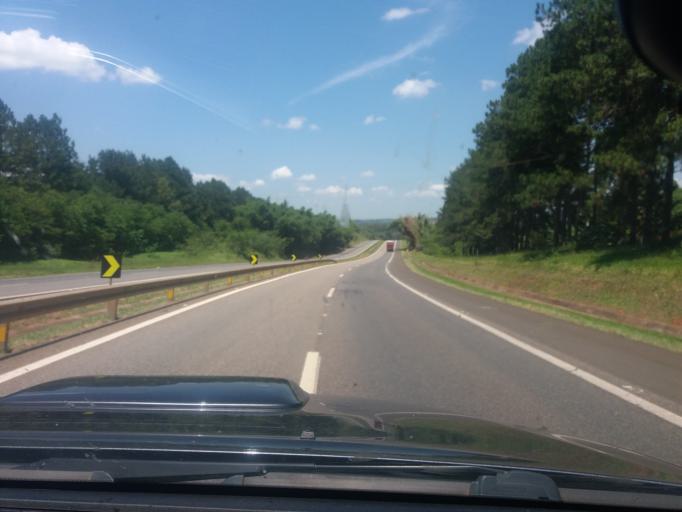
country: BR
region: Sao Paulo
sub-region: Tatui
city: Tatui
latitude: -23.3655
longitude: -47.9019
